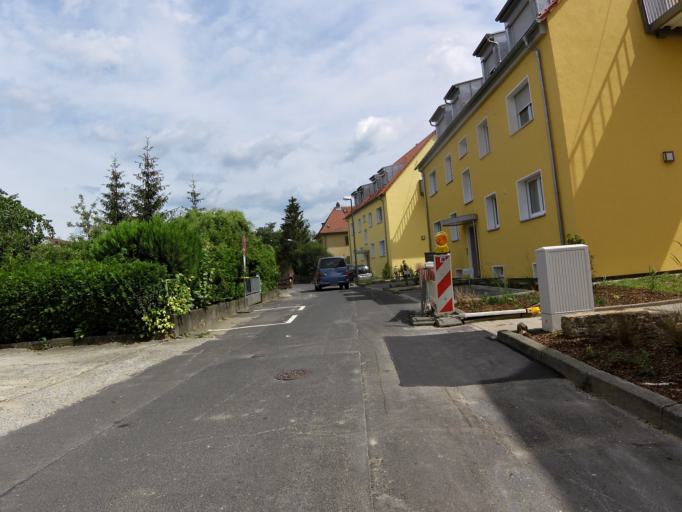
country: DE
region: Bavaria
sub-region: Regierungsbezirk Unterfranken
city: Wuerzburg
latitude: 49.7903
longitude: 9.9616
